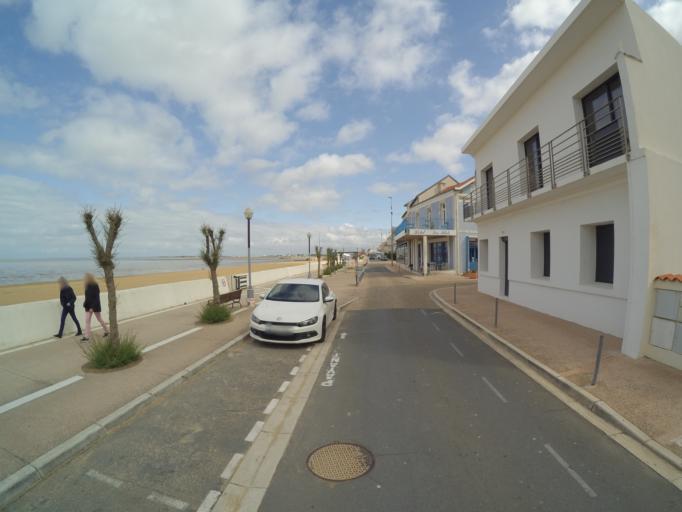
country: FR
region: Poitou-Charentes
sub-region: Departement de la Charente-Maritime
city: Chatelaillon-Plage
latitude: 46.0746
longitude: -1.0935
